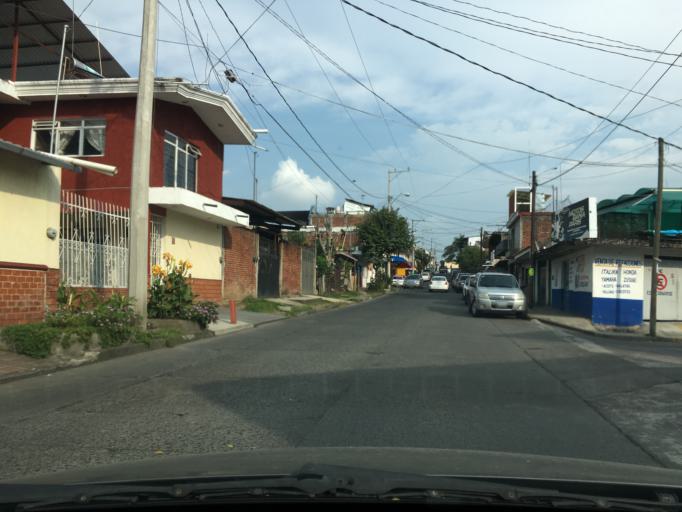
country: MX
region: Michoacan
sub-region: Uruapan
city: Uruapan
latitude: 19.4088
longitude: -102.0608
